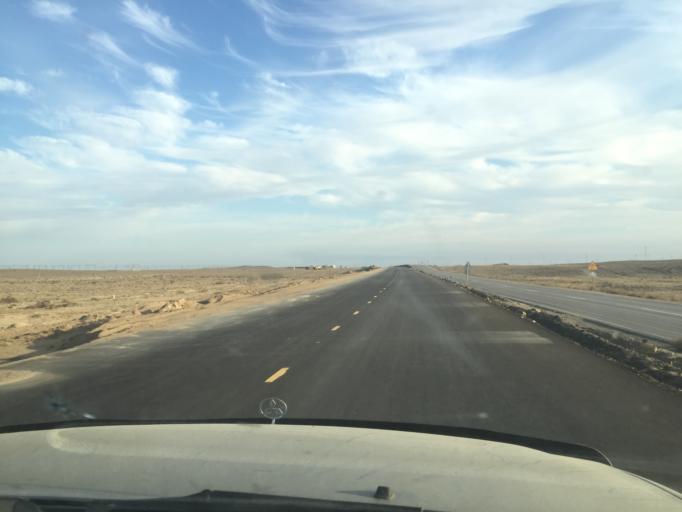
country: KZ
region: Almaty Oblysy
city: Ulken
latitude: 45.2381
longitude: 73.8313
